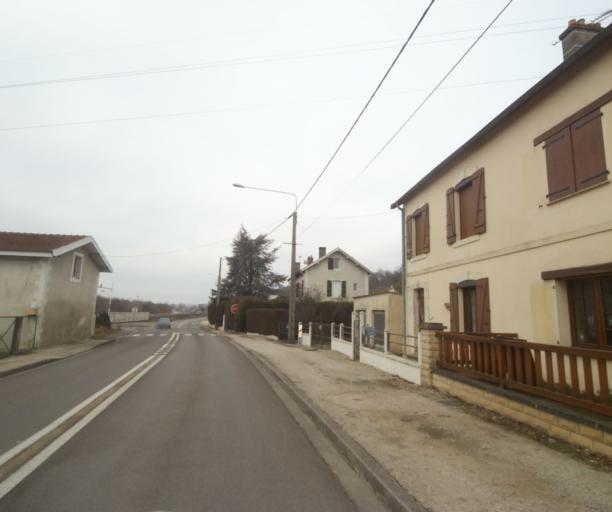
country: FR
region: Lorraine
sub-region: Departement de la Meuse
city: Ancerville
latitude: 48.6284
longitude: 4.9927
